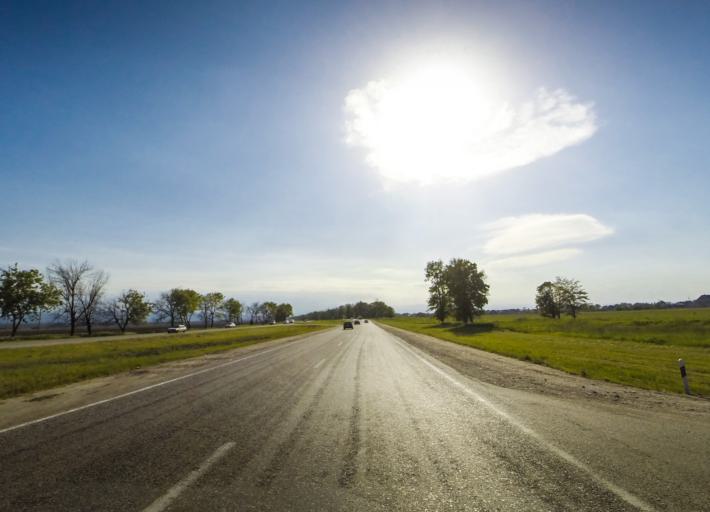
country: RU
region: Kabardino-Balkariya
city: Nartan
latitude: 43.5019
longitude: 43.7204
